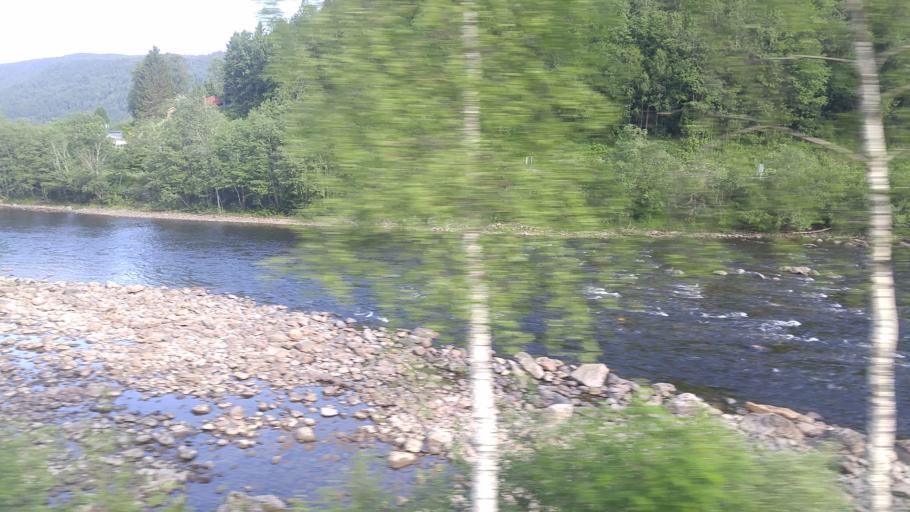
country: NO
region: Nord-Trondelag
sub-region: Levanger
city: Levanger
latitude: 63.4556
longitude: 11.4129
